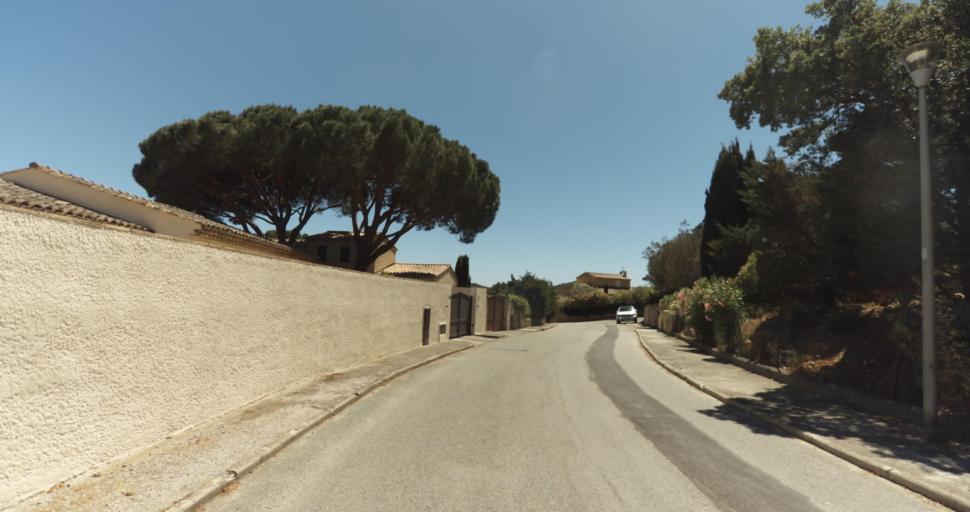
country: FR
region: Provence-Alpes-Cote d'Azur
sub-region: Departement du Var
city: Gassin
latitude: 43.2474
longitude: 6.5697
